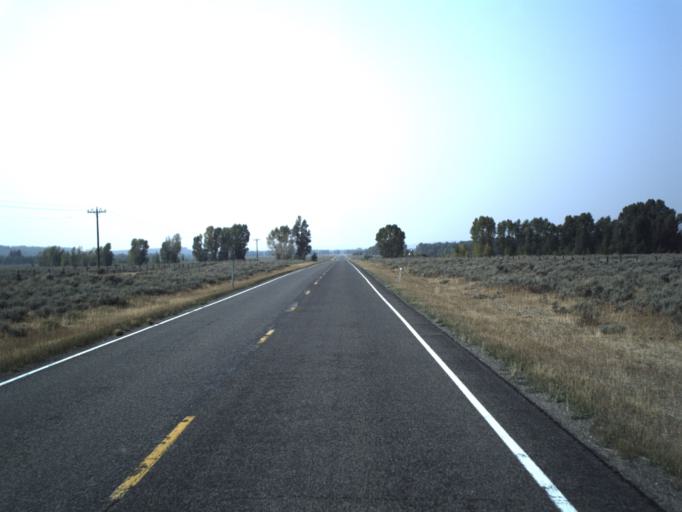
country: US
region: Wyoming
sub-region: Uinta County
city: Evanston
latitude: 40.9723
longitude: -110.8504
